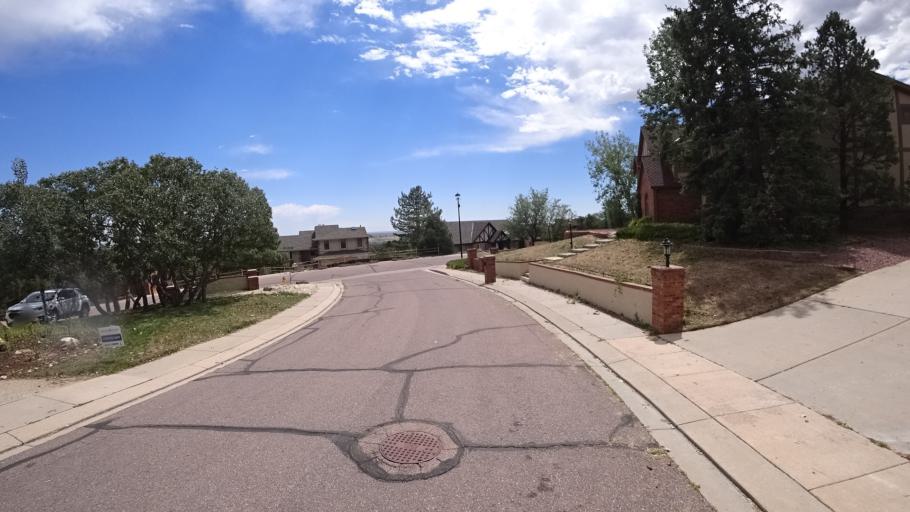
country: US
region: Colorado
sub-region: El Paso County
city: Stratmoor
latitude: 38.7692
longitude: -104.8233
